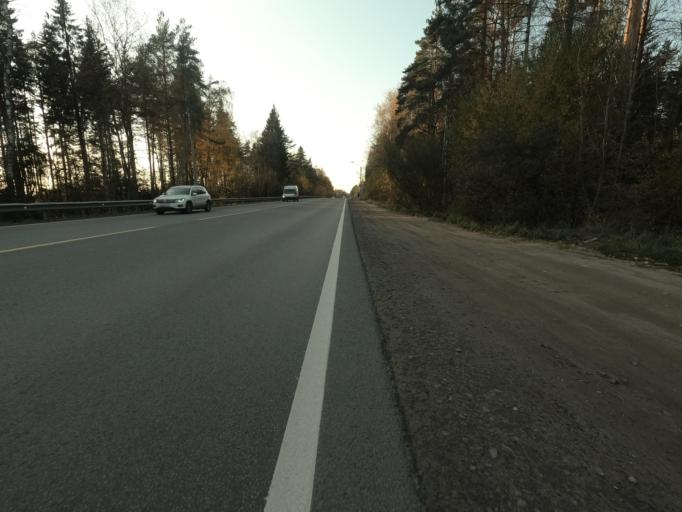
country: RU
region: St.-Petersburg
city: Pesochnyy
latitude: 60.1791
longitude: 30.1438
